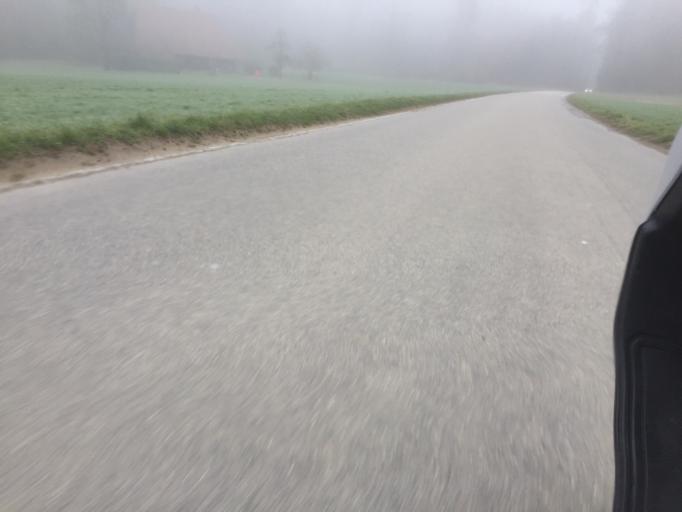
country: CH
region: Bern
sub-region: Seeland District
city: Grossaffoltern
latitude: 47.0972
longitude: 7.3653
